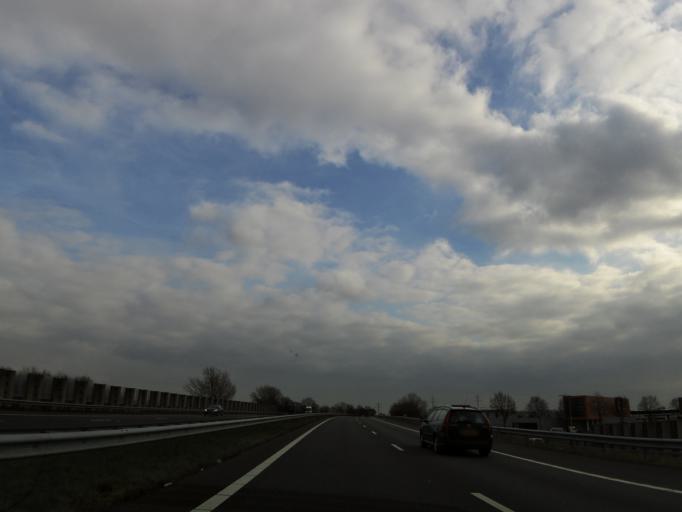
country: NL
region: Limburg
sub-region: Gemeente Nederweert
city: Nederweert
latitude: 51.2778
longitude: 5.7346
